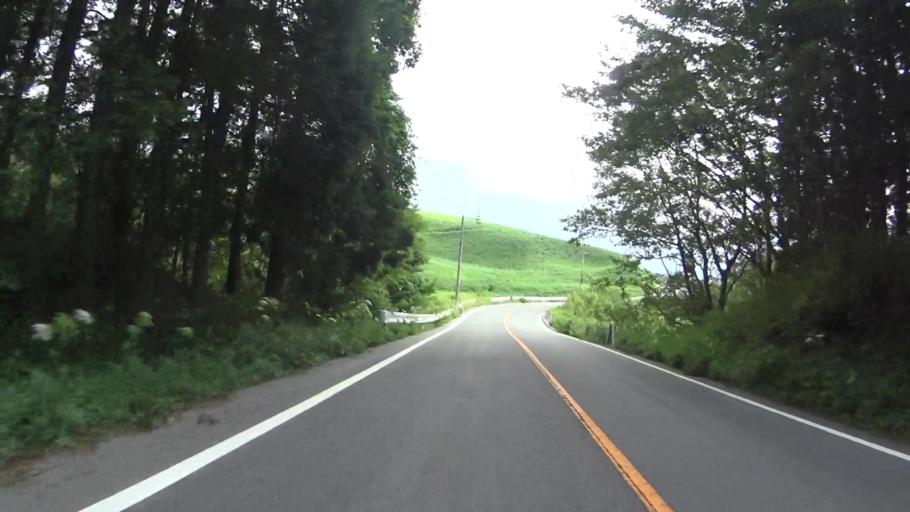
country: JP
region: Kumamoto
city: Aso
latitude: 32.8976
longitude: 131.0283
